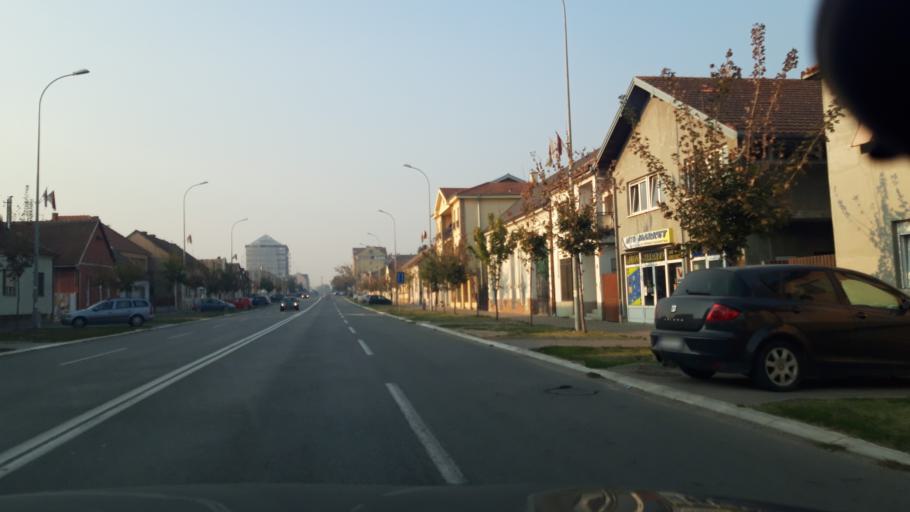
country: RS
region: Autonomna Pokrajina Vojvodina
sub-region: Sremski Okrug
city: Ingija
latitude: 45.0445
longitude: 20.0843
